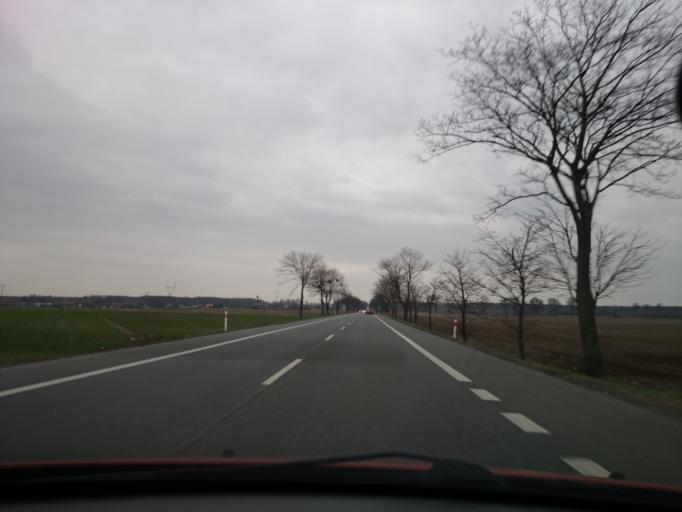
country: PL
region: Opole Voivodeship
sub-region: Powiat opolski
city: Niemodlin
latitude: 50.6248
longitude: 17.5798
